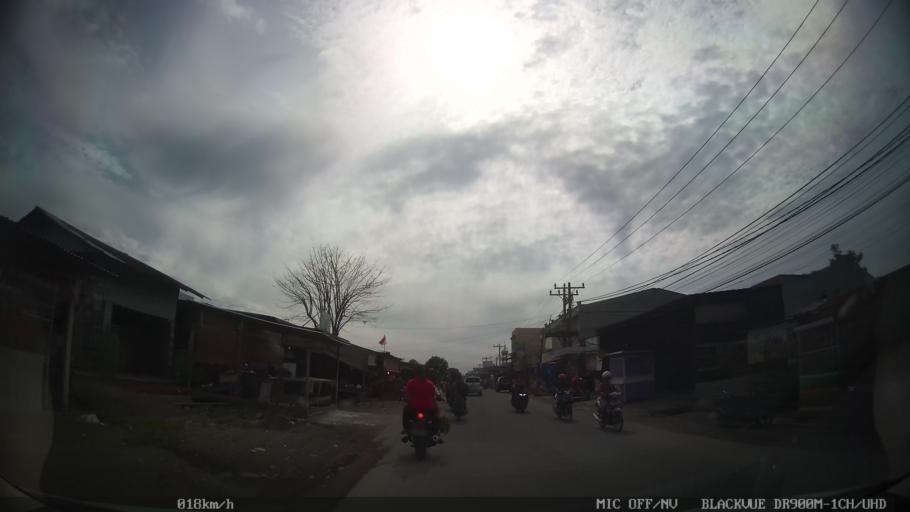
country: ID
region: North Sumatra
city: Medan
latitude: 3.6209
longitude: 98.7237
